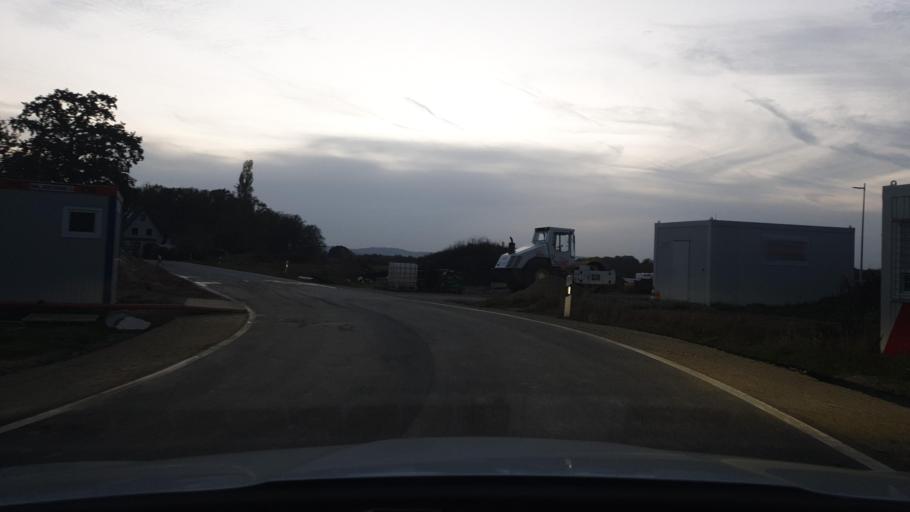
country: DE
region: North Rhine-Westphalia
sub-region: Regierungsbezirk Detmold
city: Bielefeld
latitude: 52.0661
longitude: 8.5786
